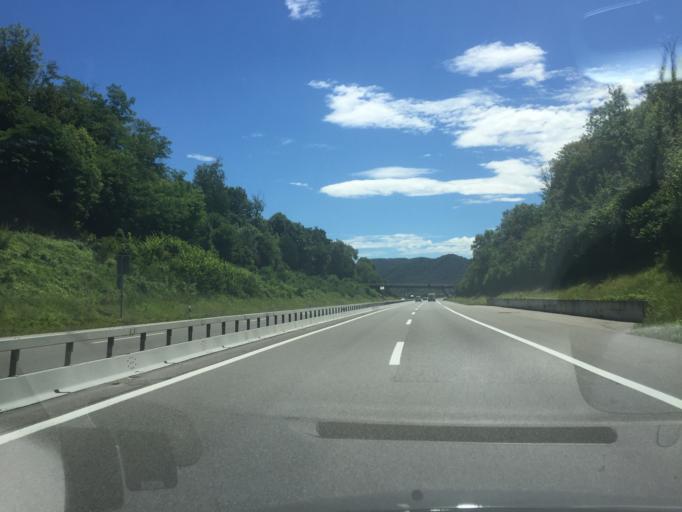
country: CH
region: Ticino
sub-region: Mendrisio District
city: Mendrisio
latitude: 45.8543
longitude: 8.9793
